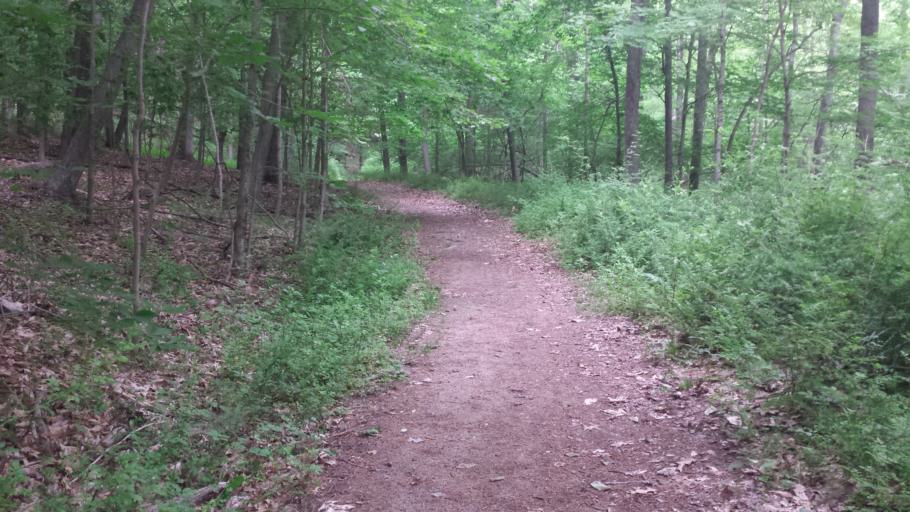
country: US
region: New York
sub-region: Westchester County
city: Pound Ridge
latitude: 41.2674
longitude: -73.5956
